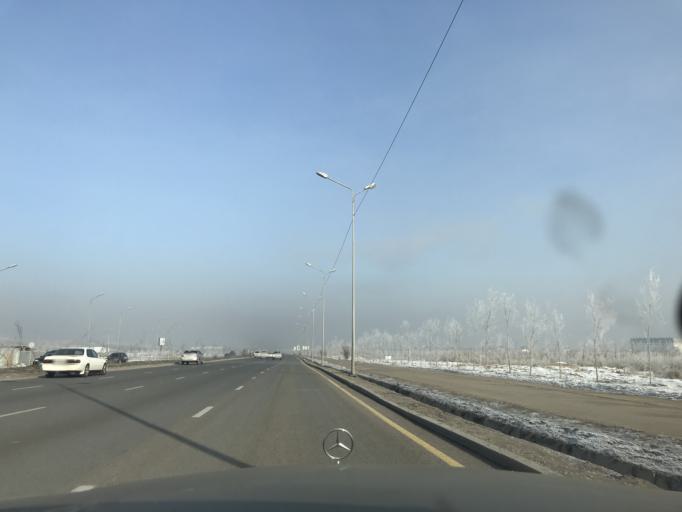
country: KZ
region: Almaty Oblysy
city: Burunday
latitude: 43.3190
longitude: 76.8339
